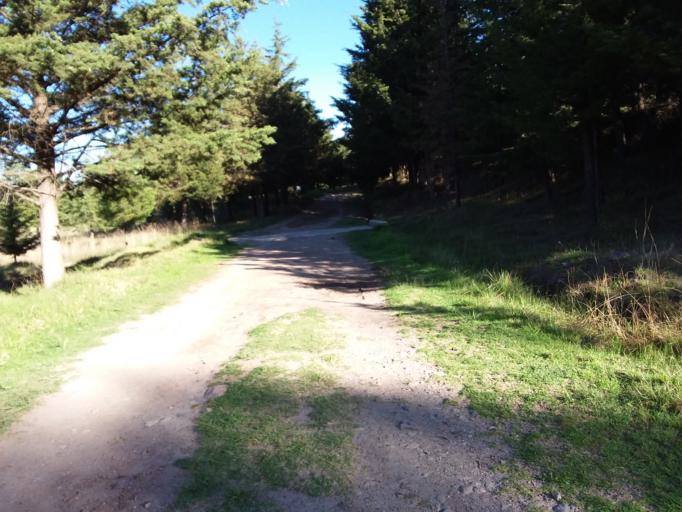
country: MX
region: Mexico
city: San Marcos Yachihuacaltepec
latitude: 19.3131
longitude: -99.6952
